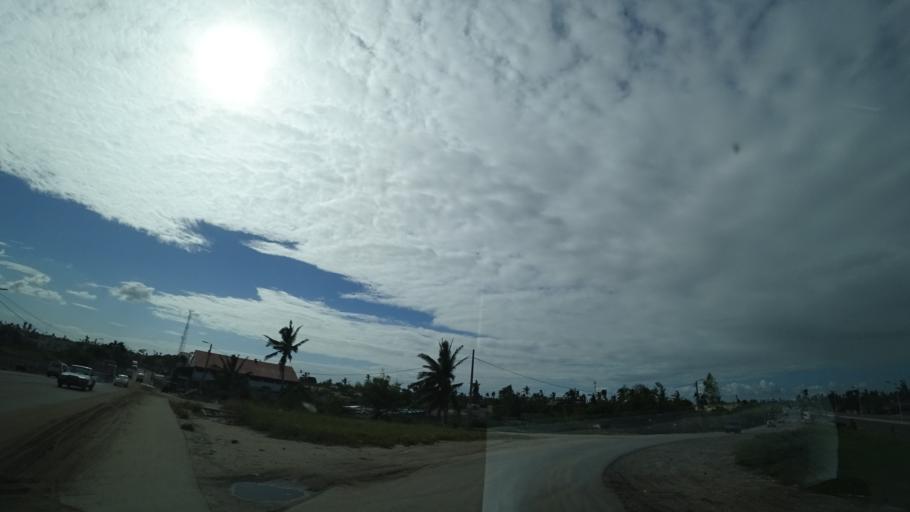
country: MZ
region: Sofala
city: Beira
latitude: -19.7825
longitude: 34.8782
